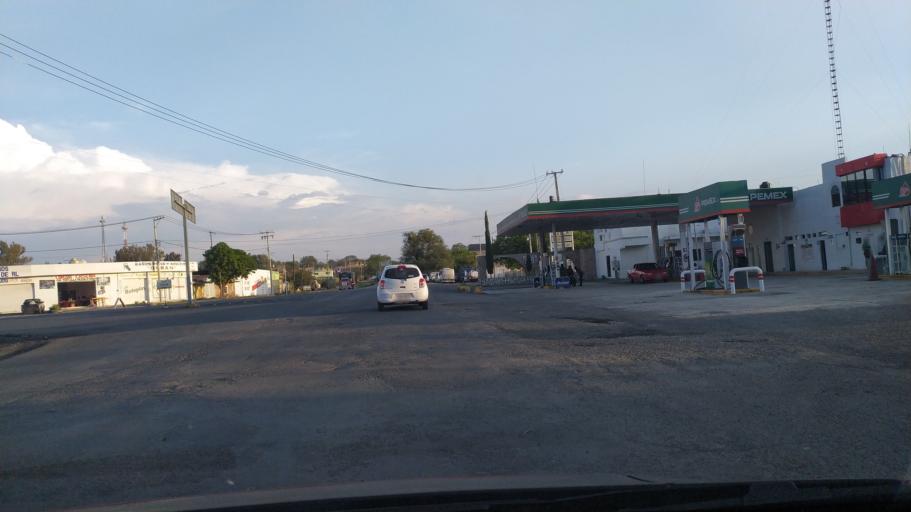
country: MX
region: Michoacan
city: Vistahermosa de Negrete
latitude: 20.2666
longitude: -102.4747
